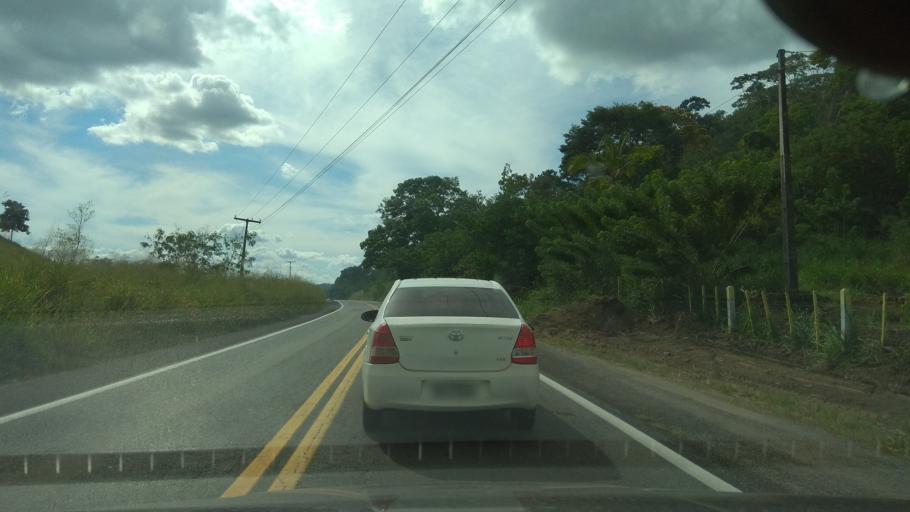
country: BR
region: Bahia
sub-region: Ipiau
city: Ipiau
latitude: -14.0797
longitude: -39.7816
